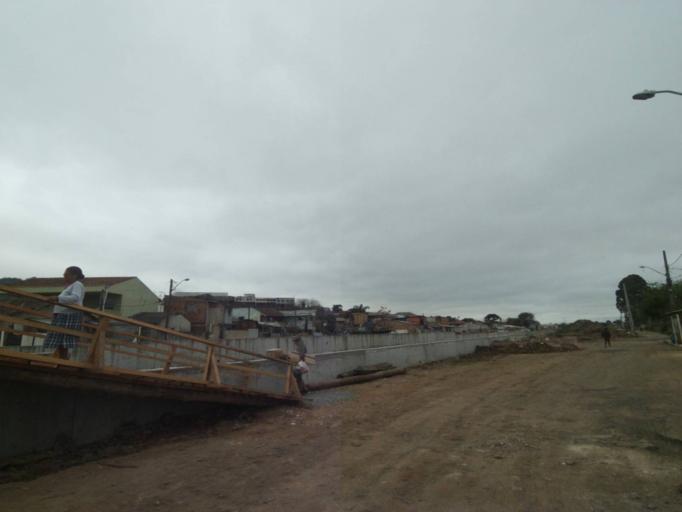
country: BR
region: Parana
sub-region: Curitiba
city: Curitiba
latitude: -25.4642
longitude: -49.2692
